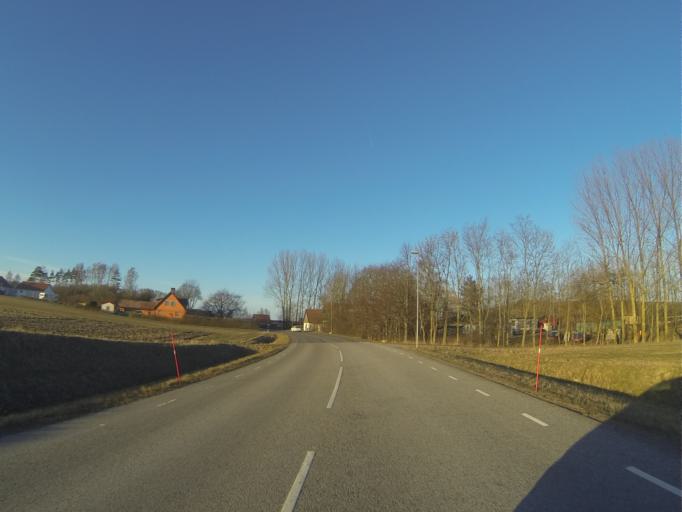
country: SE
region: Skane
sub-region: Malmo
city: Oxie
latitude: 55.5611
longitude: 13.1090
